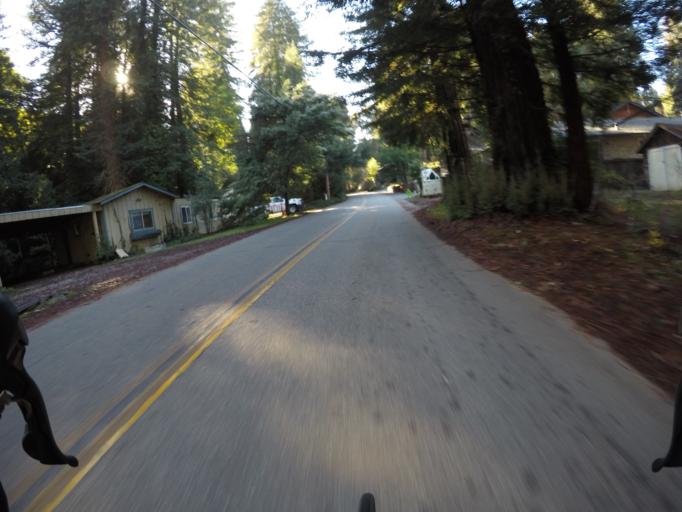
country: US
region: California
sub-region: Santa Cruz County
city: Felton
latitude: 37.0428
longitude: -122.0760
